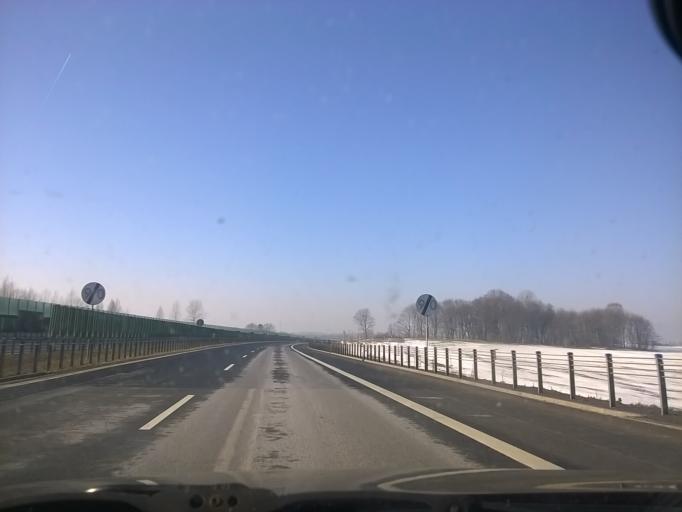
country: PL
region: Warmian-Masurian Voivodeship
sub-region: Powiat olsztynski
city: Biskupiec
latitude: 53.8465
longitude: 20.9834
